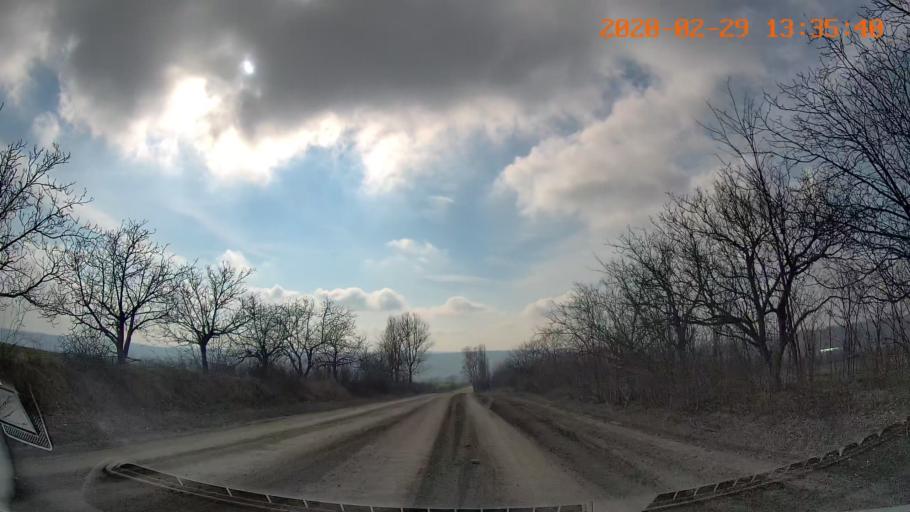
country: MD
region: Telenesti
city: Camenca
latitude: 47.8649
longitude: 28.6115
